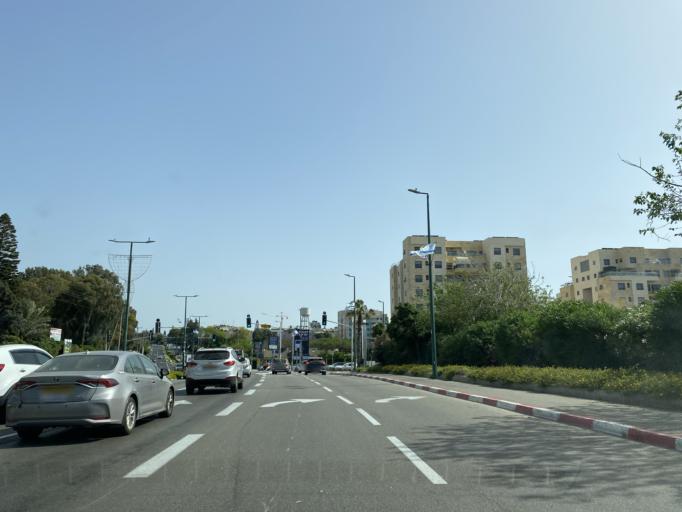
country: IL
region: Central District
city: Ra'anana
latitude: 32.1768
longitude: 34.8514
